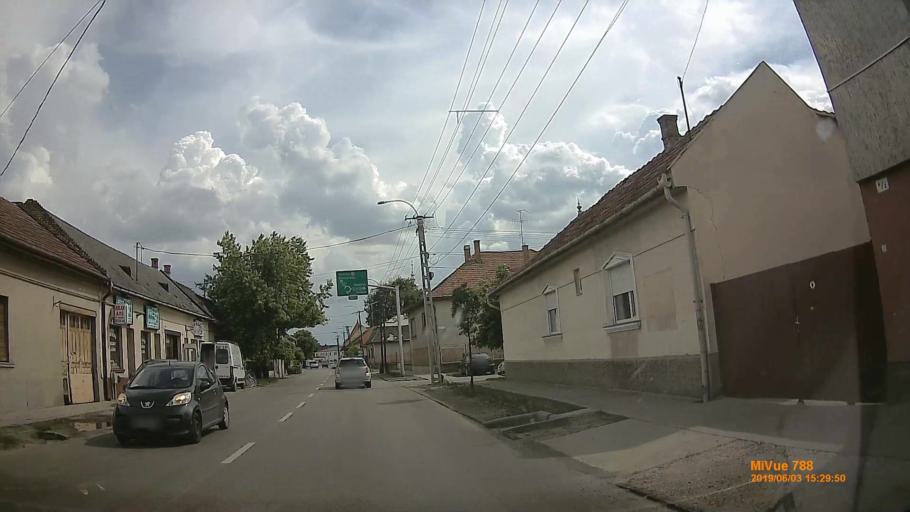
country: HU
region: Bacs-Kiskun
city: Soltvadkert
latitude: 46.5830
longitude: 19.3937
